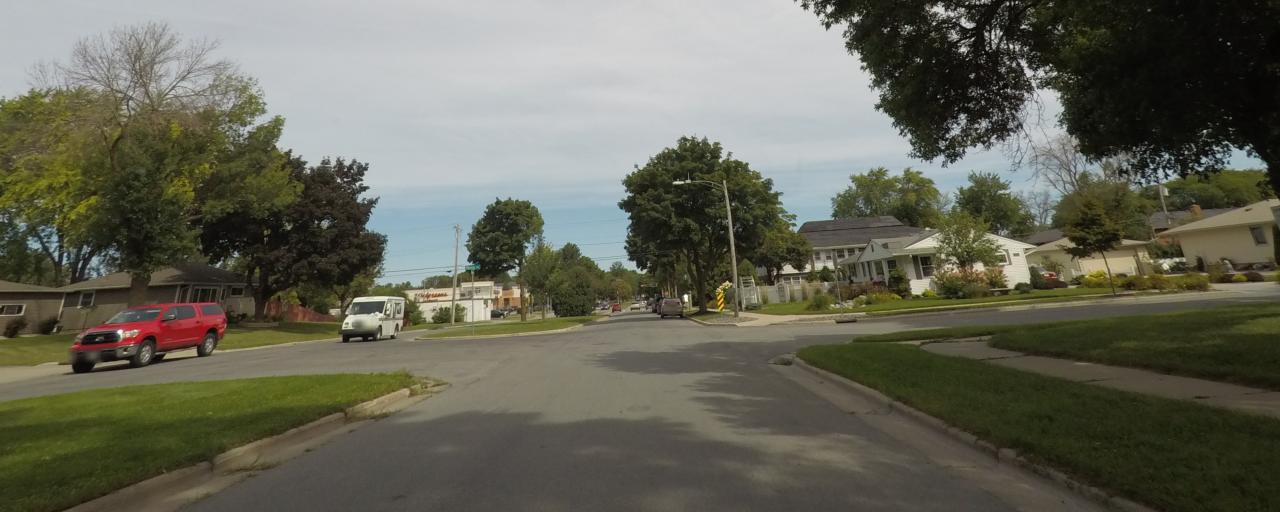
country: US
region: Wisconsin
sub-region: Dane County
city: Monona
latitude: 43.0827
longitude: -89.3029
